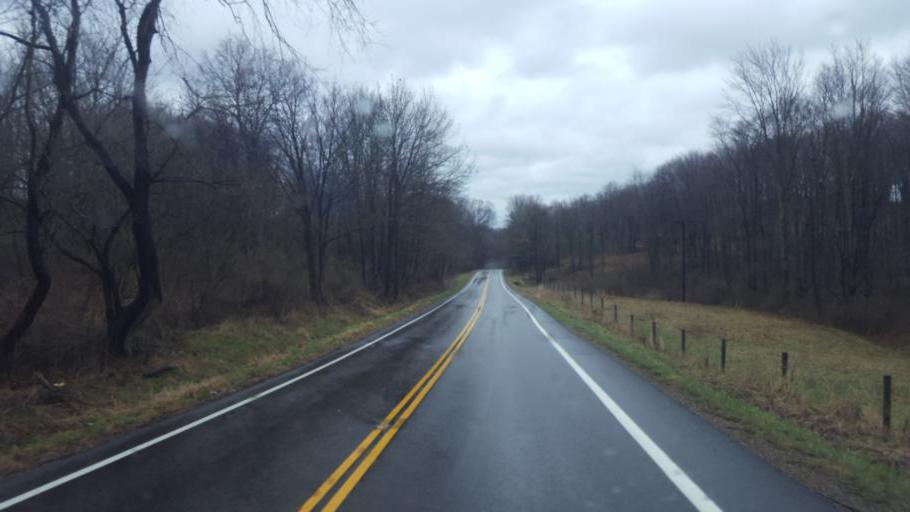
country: US
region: Ohio
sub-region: Sandusky County
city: Bellville
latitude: 40.6221
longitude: -82.3982
